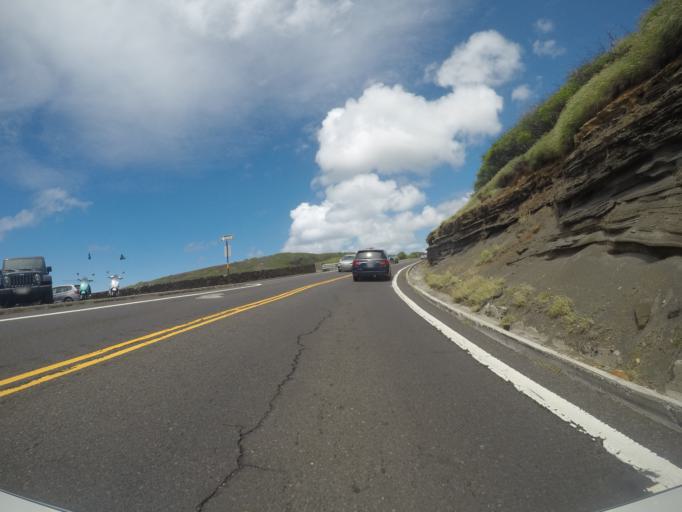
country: US
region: Hawaii
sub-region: Honolulu County
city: Waimanalo Beach
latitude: 21.2766
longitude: -157.6857
